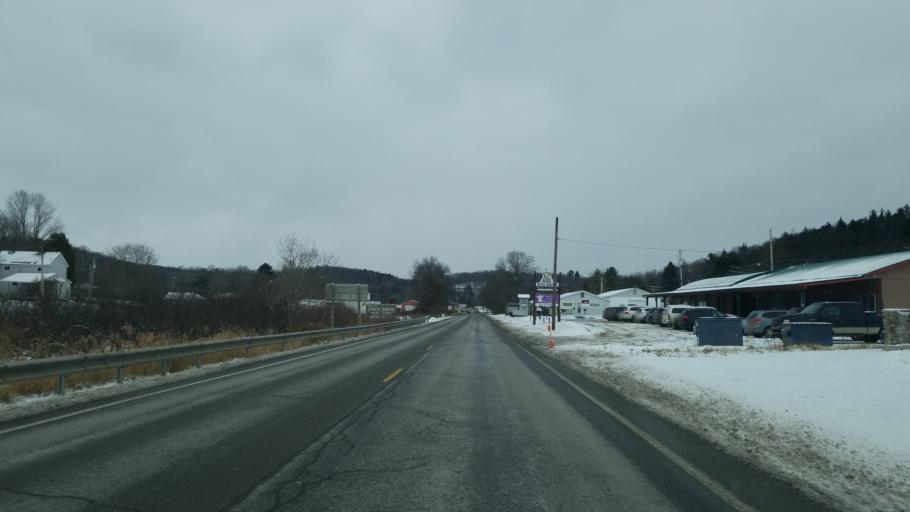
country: US
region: Pennsylvania
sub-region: Clearfield County
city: Sandy
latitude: 41.0875
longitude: -78.7667
